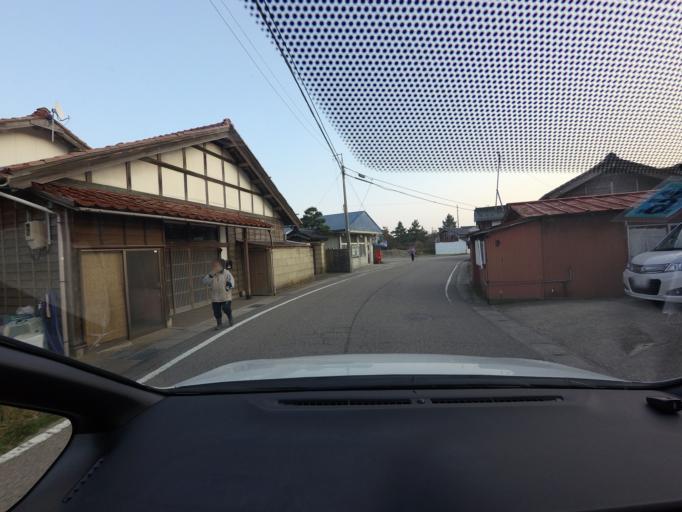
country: JP
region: Ishikawa
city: Nanao
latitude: 37.1572
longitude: 137.0478
